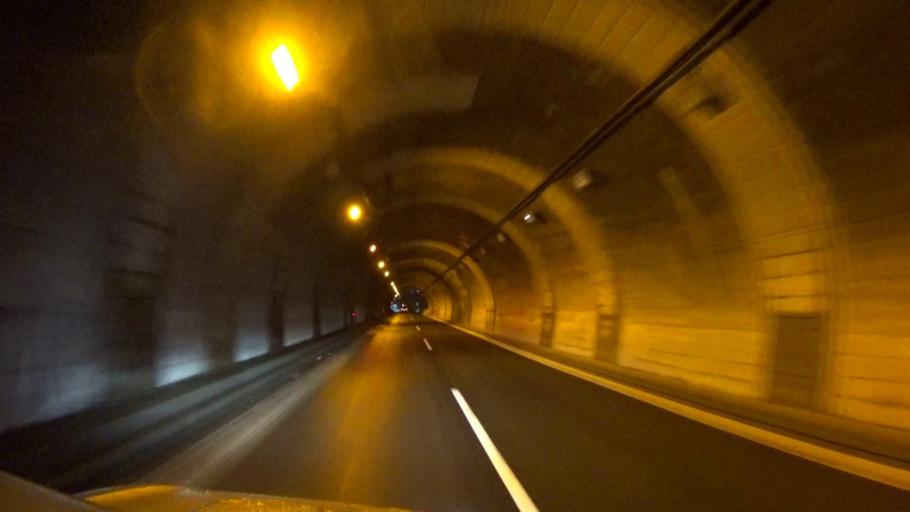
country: JP
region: Hokkaido
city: Otaru
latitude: 43.1747
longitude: 141.0292
